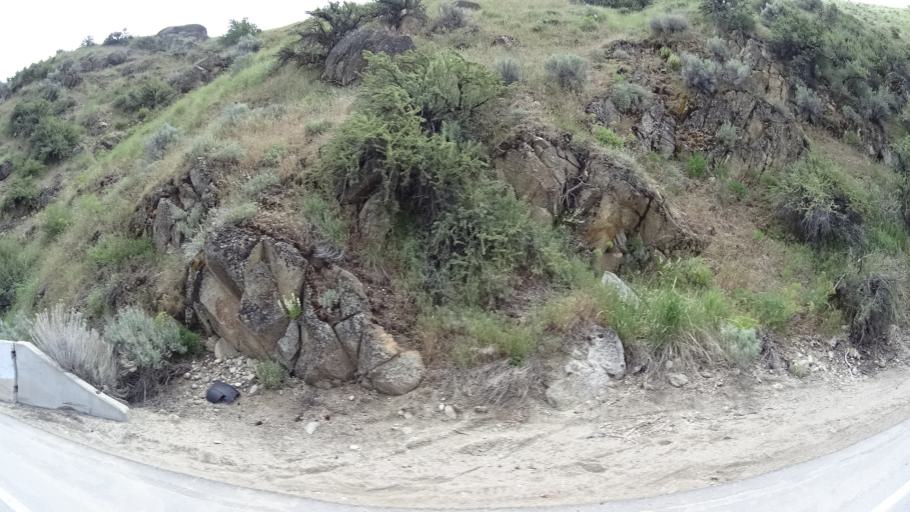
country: US
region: Idaho
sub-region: Ada County
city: Boise
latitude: 43.6872
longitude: -116.1800
